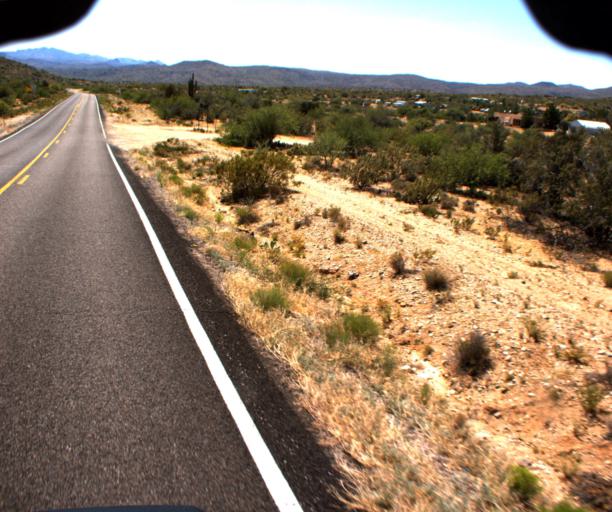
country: US
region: Arizona
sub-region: Yavapai County
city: Bagdad
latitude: 34.4826
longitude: -113.1905
